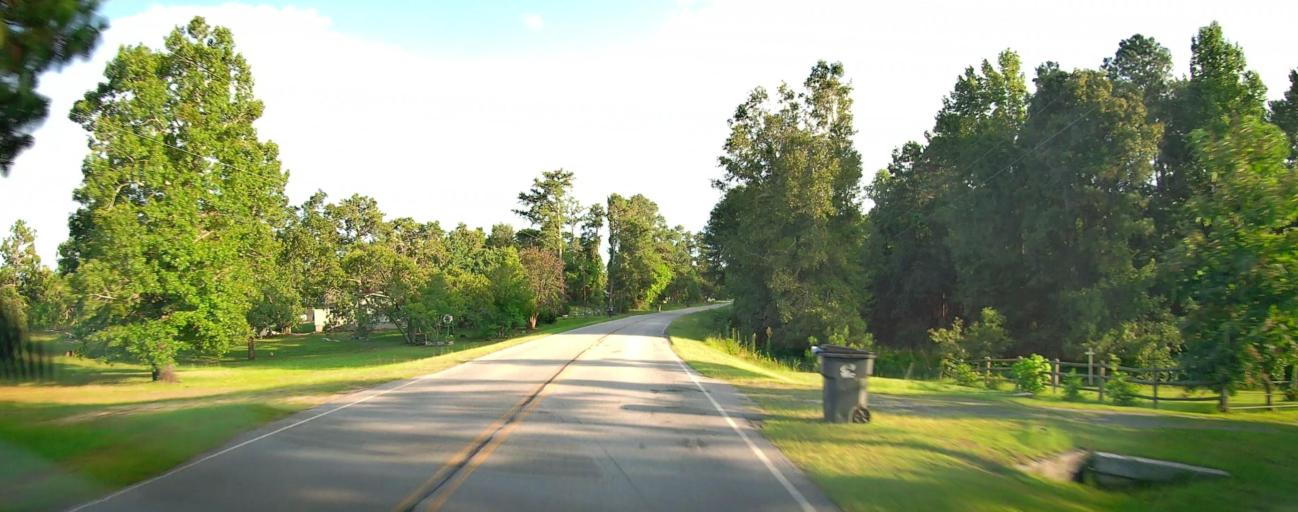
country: US
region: Georgia
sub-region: Peach County
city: Byron
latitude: 32.6998
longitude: -83.8501
